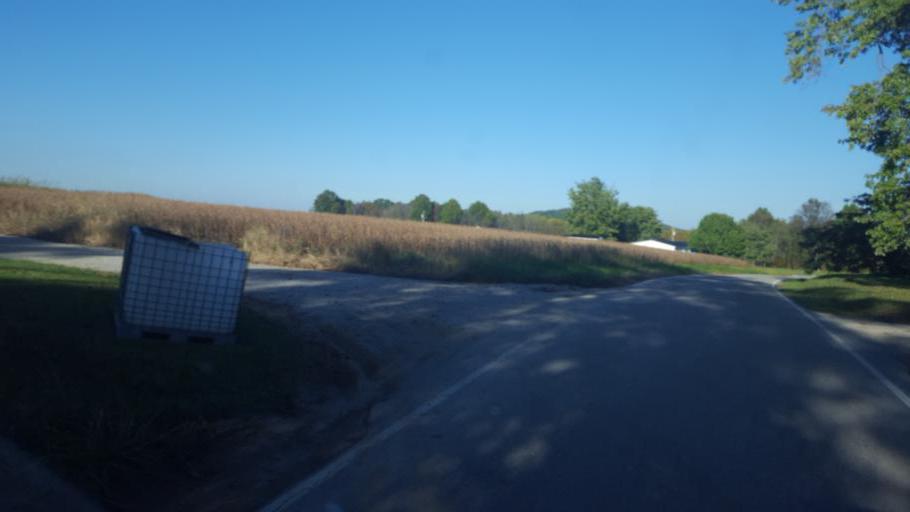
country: US
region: Kentucky
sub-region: Fleming County
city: Flemingsburg
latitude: 38.4918
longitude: -83.5856
